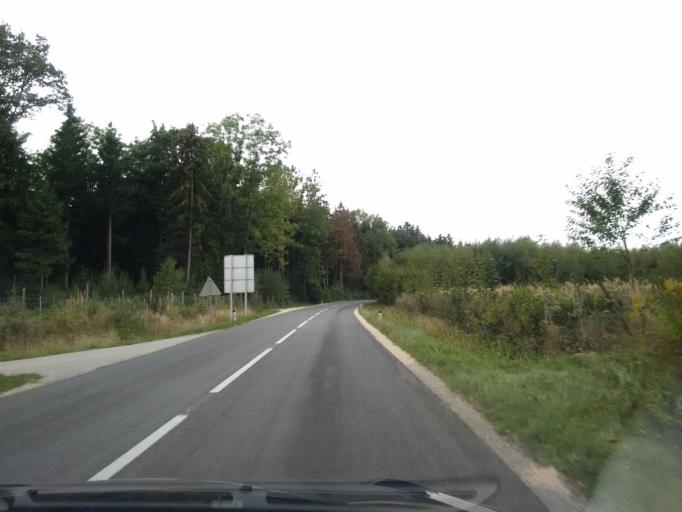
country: AT
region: Upper Austria
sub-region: Wels-Land
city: Marchtrenk
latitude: 48.1552
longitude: 14.1542
